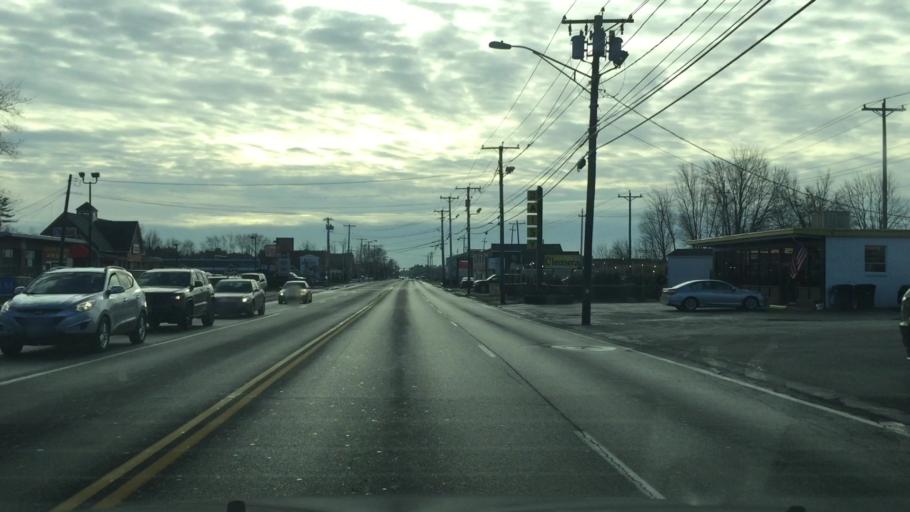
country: US
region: New Hampshire
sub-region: Rockingham County
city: Salem
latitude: 42.7815
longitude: -71.2292
